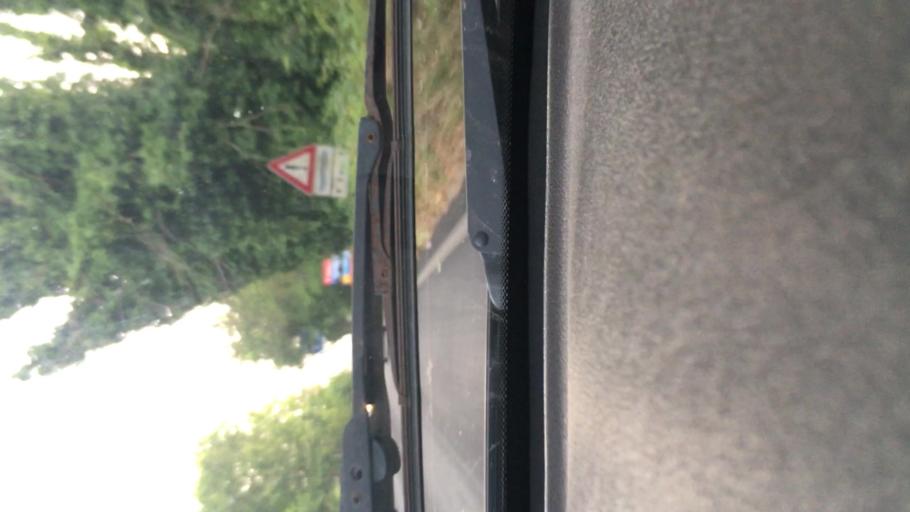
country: IT
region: Latium
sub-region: Citta metropolitana di Roma Capitale
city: Vitinia
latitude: 41.8157
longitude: 12.4306
